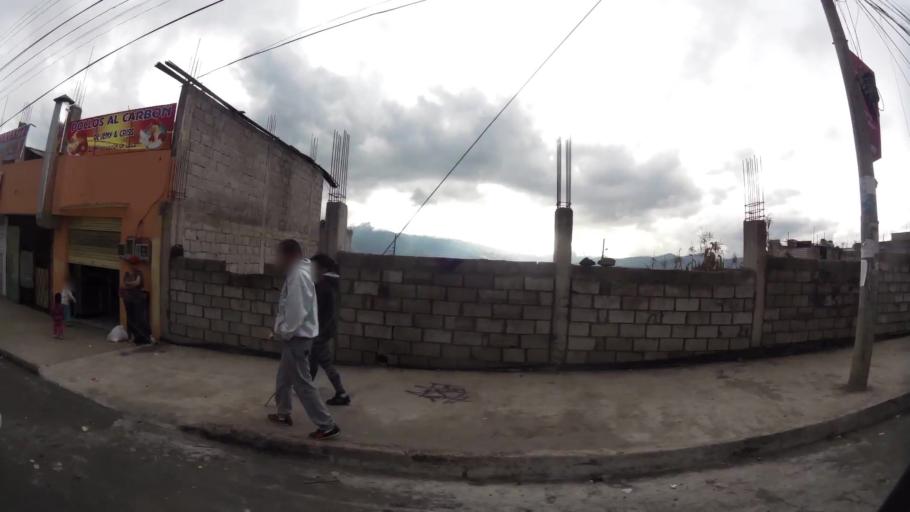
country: EC
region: Pichincha
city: Sangolqui
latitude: -0.3097
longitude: -78.5262
